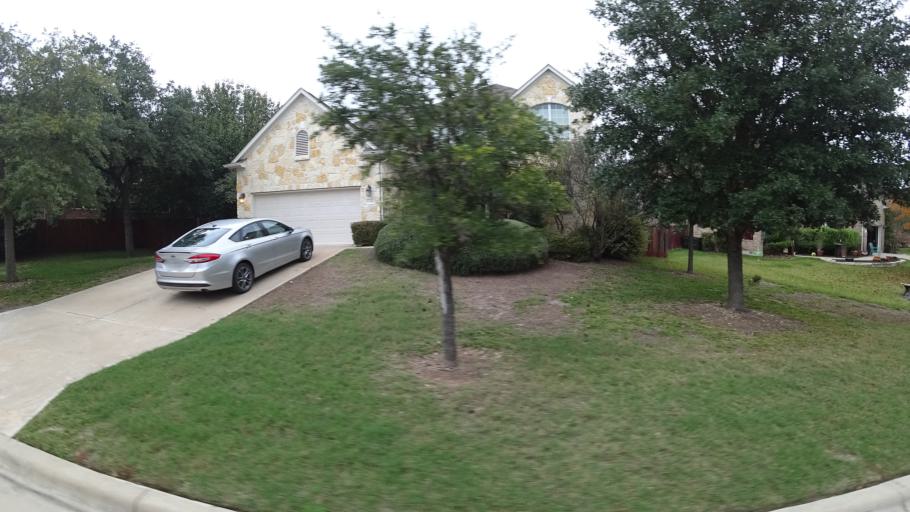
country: US
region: Texas
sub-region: Travis County
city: Hudson Bend
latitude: 30.3599
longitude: -97.9004
